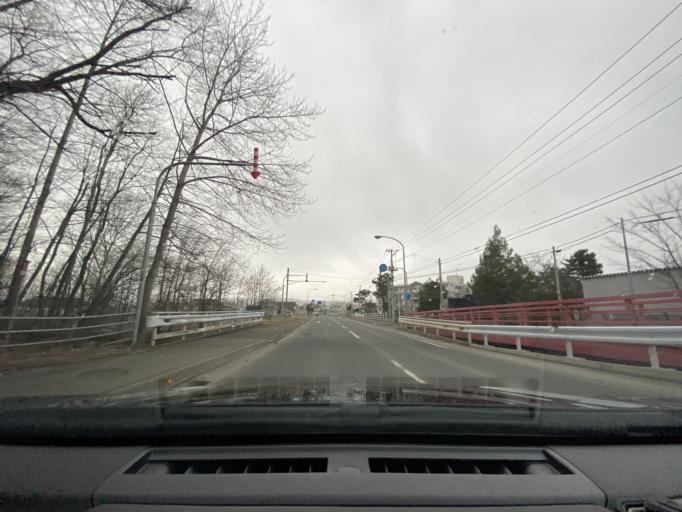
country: JP
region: Hokkaido
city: Kitami
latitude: 43.7970
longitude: 143.9164
